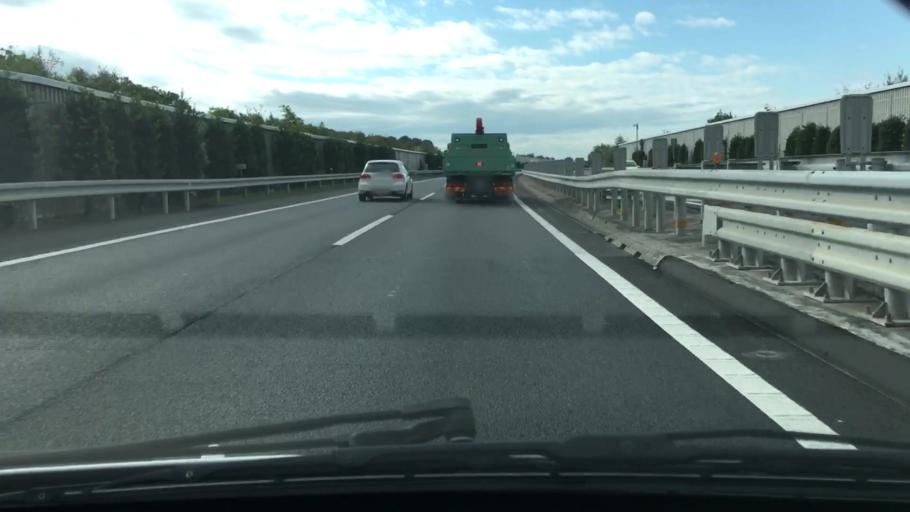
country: JP
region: Chiba
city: Ichihara
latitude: 35.5411
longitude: 140.1395
